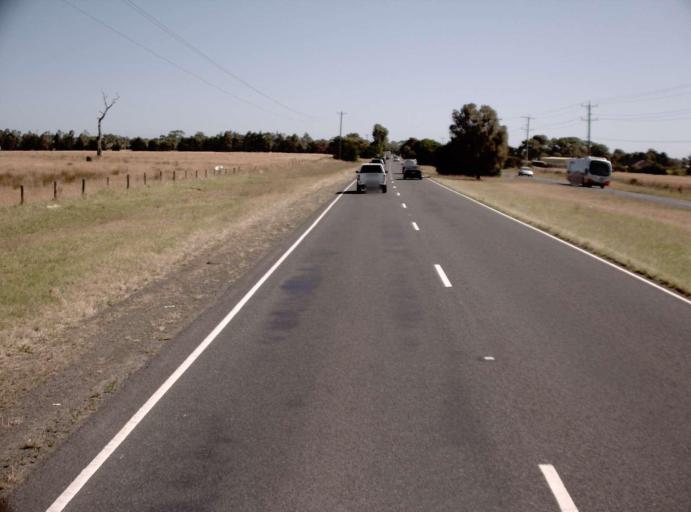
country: AU
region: Victoria
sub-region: Frankston
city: Sandhurst
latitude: -38.0807
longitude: 145.1878
